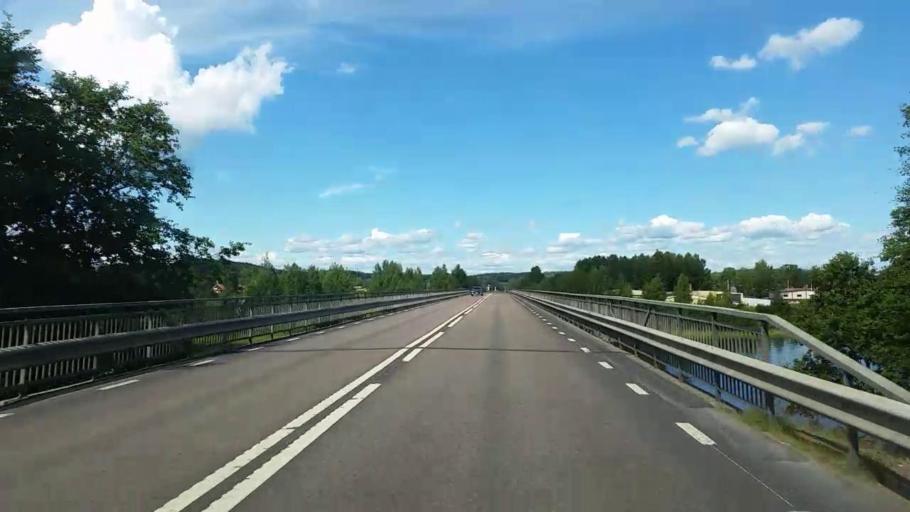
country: SE
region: Dalarna
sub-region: Leksand Municipality
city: Leksand
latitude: 60.7276
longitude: 15.0097
